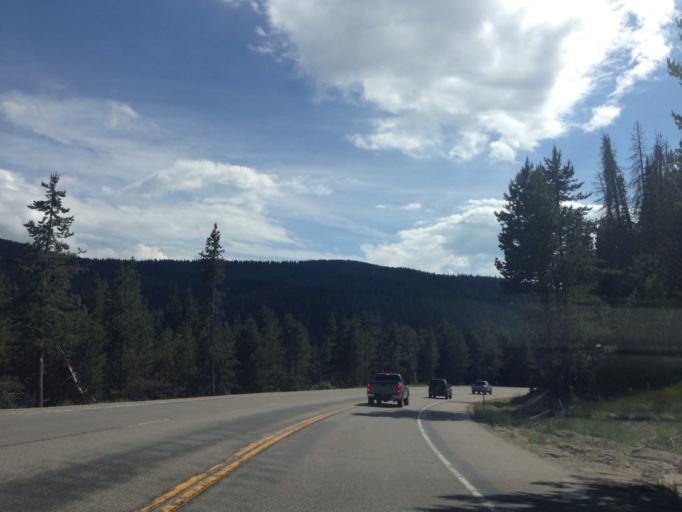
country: US
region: Colorado
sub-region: Routt County
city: Steamboat Springs
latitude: 40.3500
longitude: -106.7438
